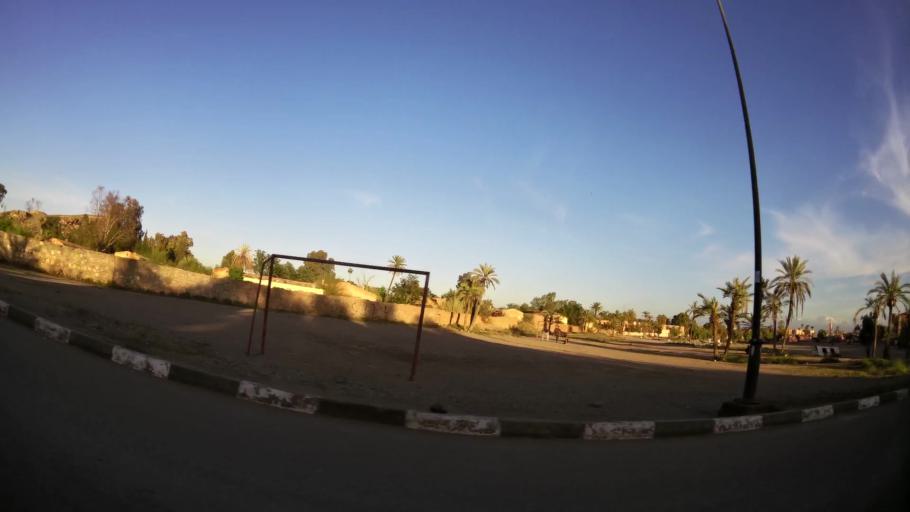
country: MA
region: Marrakech-Tensift-Al Haouz
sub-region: Marrakech
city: Marrakesh
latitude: 31.6407
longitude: -8.0355
